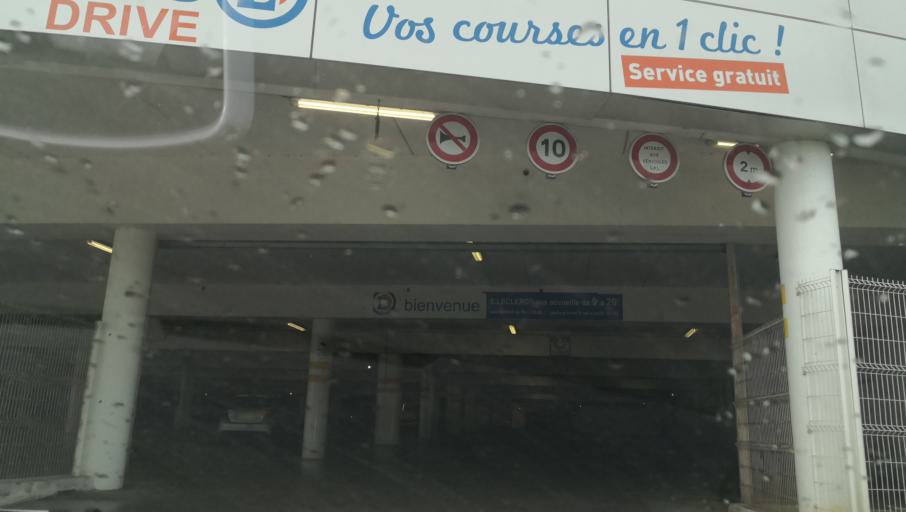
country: FR
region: Limousin
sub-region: Departement de la Haute-Vienne
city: Couzeix
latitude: 45.8686
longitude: 1.2706
